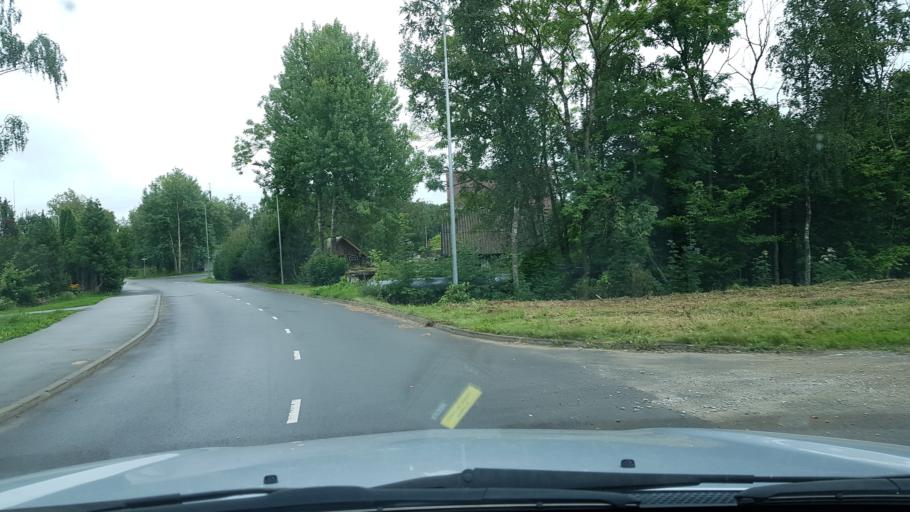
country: EE
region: Harju
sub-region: Rae vald
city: Jueri
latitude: 59.3560
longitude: 24.9177
